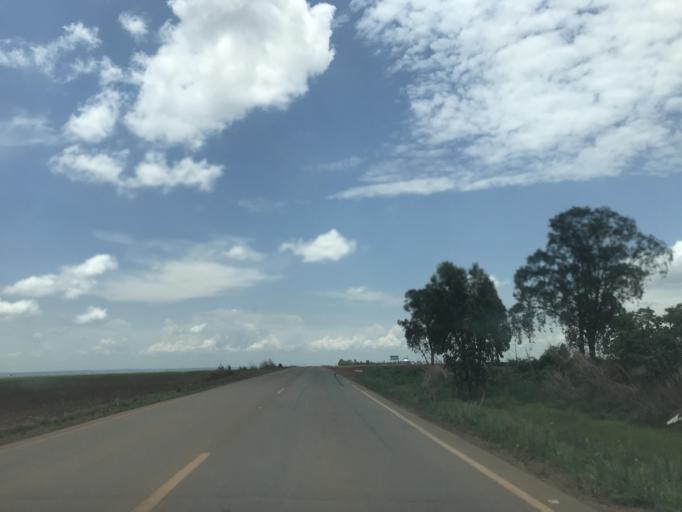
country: BR
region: Goias
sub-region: Vianopolis
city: Vianopolis
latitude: -16.5361
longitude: -48.2523
